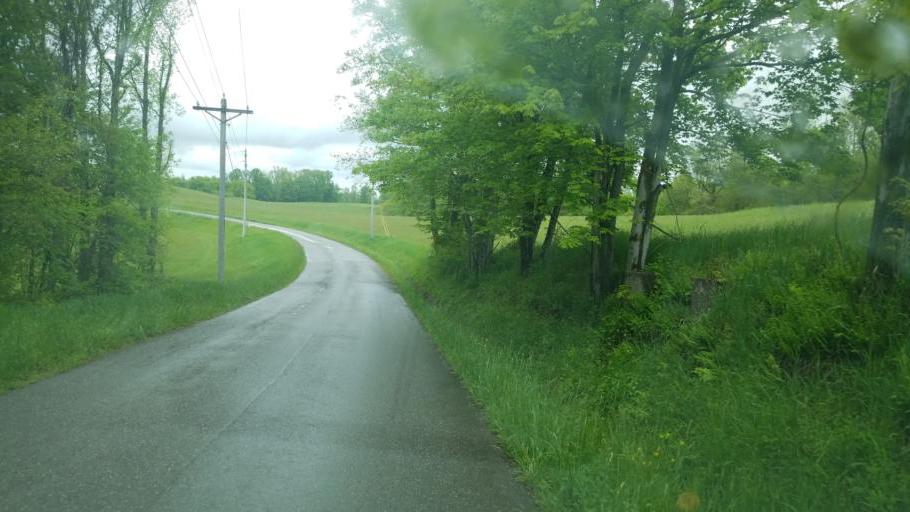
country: US
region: Ohio
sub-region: Tuscarawas County
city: Rockford
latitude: 40.3974
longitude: -81.1892
